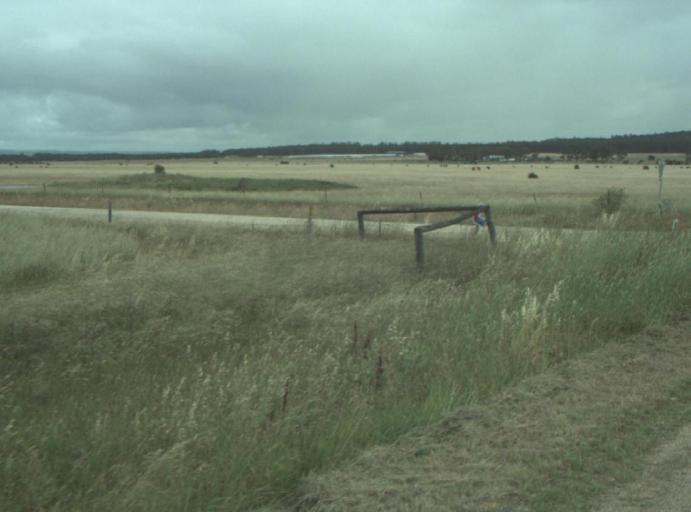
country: AU
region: Victoria
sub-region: Greater Geelong
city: Lara
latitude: -37.9821
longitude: 144.4225
